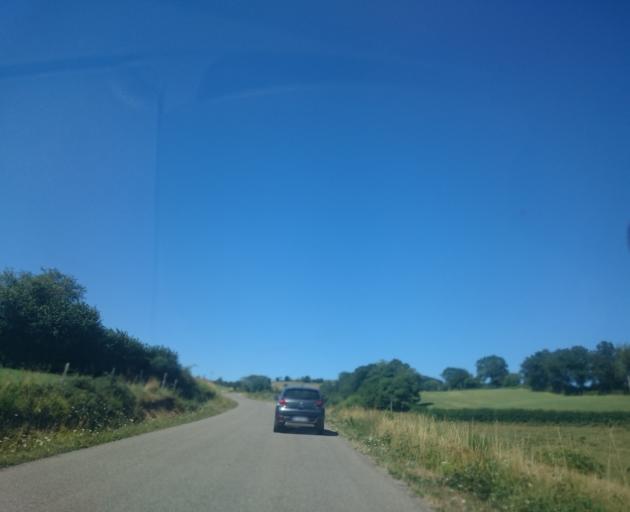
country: FR
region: Auvergne
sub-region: Departement du Cantal
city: Saint-Mamet-la-Salvetat
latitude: 44.8011
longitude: 2.3650
